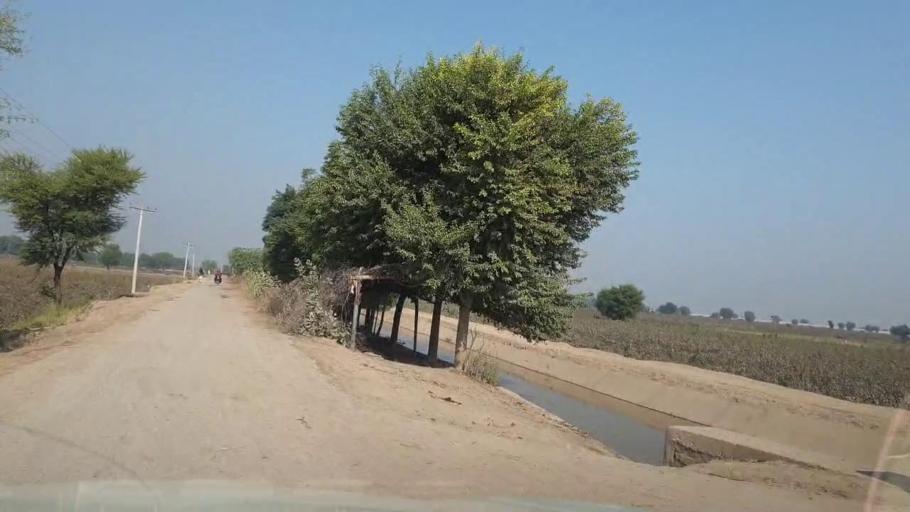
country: PK
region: Sindh
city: Bhan
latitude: 26.5433
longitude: 67.7738
